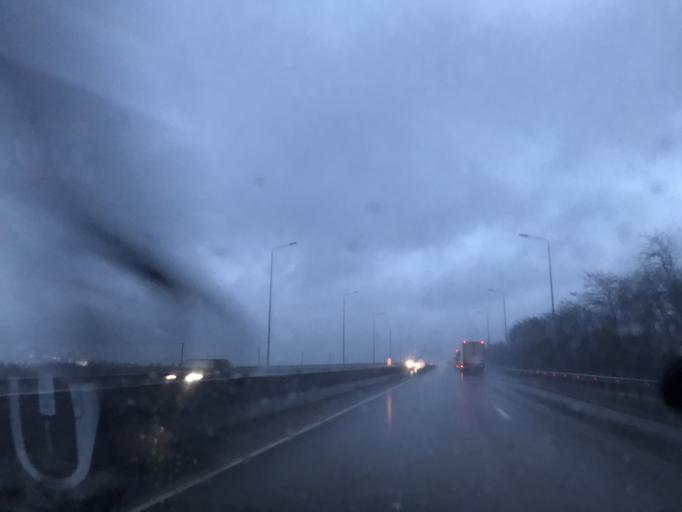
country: RU
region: Rostov
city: Samarskoye
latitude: 46.9601
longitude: 39.7174
